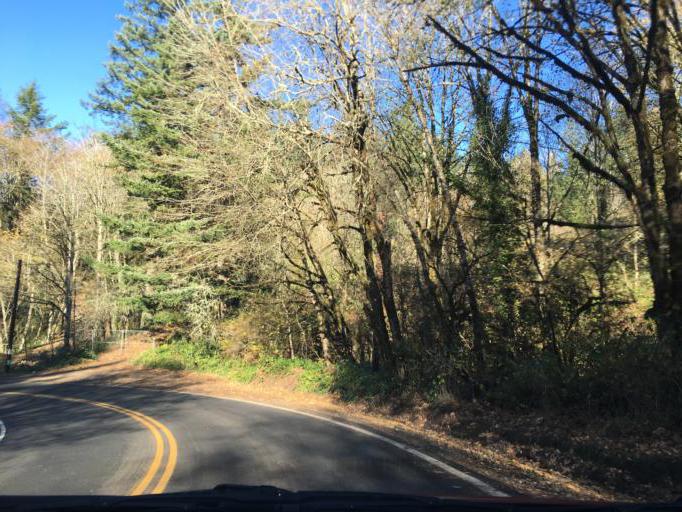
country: US
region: Oregon
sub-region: Washington County
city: Oak Hills
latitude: 45.5835
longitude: -122.8058
